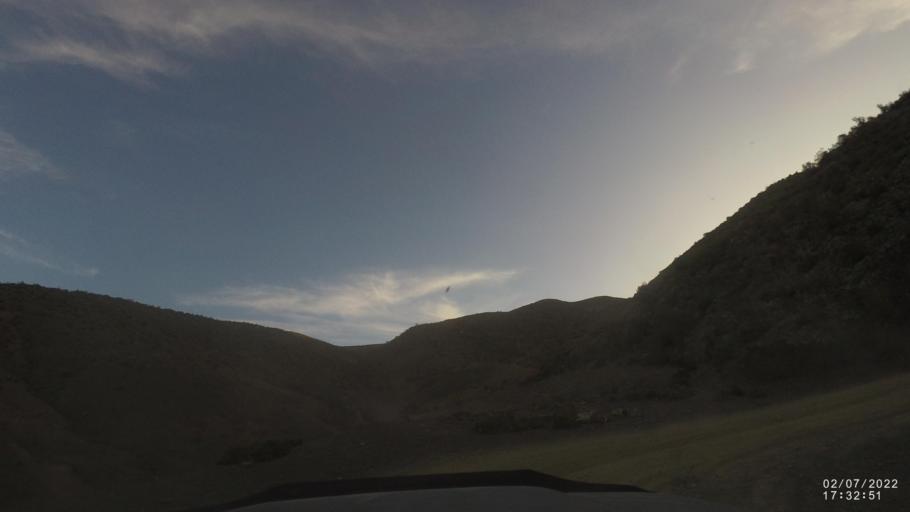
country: BO
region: Cochabamba
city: Irpa Irpa
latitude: -17.8849
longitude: -66.6190
